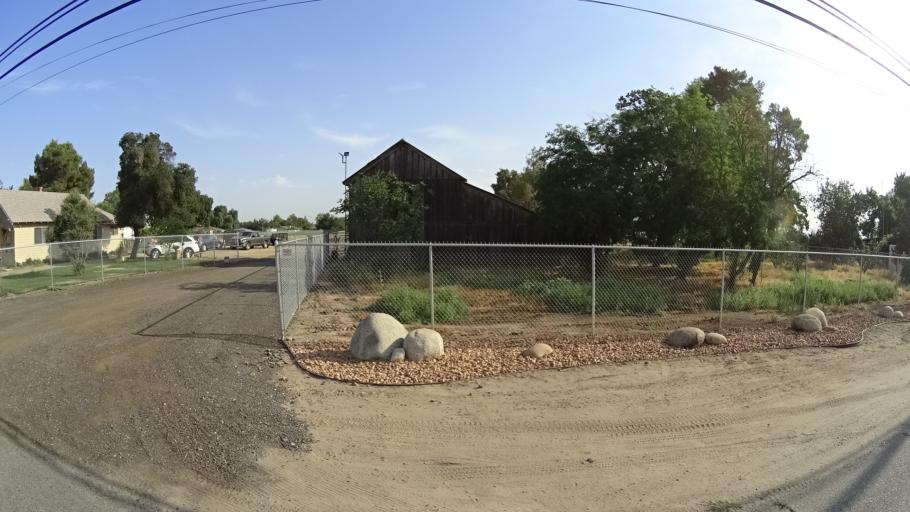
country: US
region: California
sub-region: Fresno County
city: West Park
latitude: 36.7500
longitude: -119.8605
